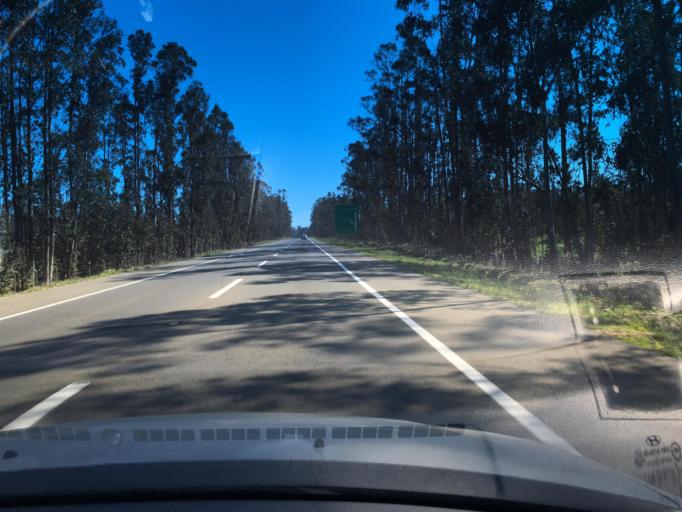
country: CL
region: Valparaiso
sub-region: San Antonio Province
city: El Tabo
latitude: -33.4019
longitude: -71.5791
